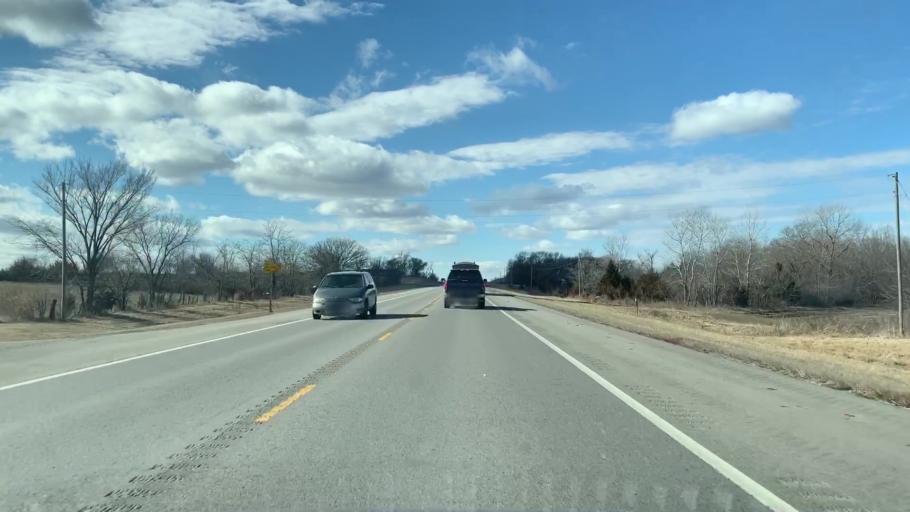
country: US
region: Kansas
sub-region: Cherokee County
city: Columbus
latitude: 37.3399
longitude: -94.8908
